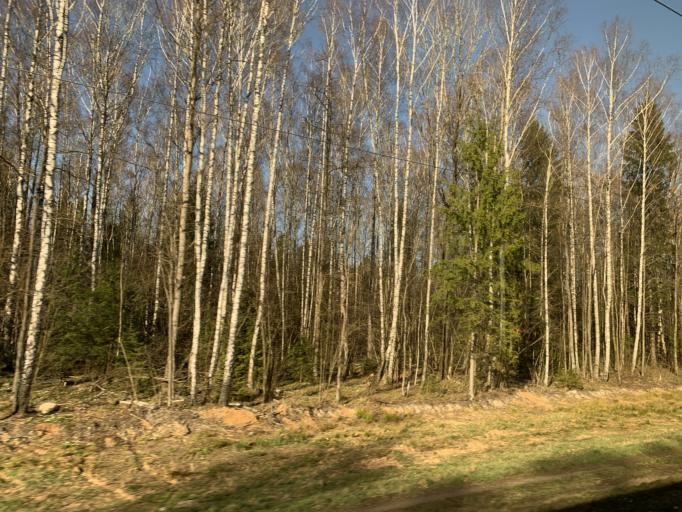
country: BY
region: Grodnenskaya
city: Smarhon'
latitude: 54.4884
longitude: 26.3063
